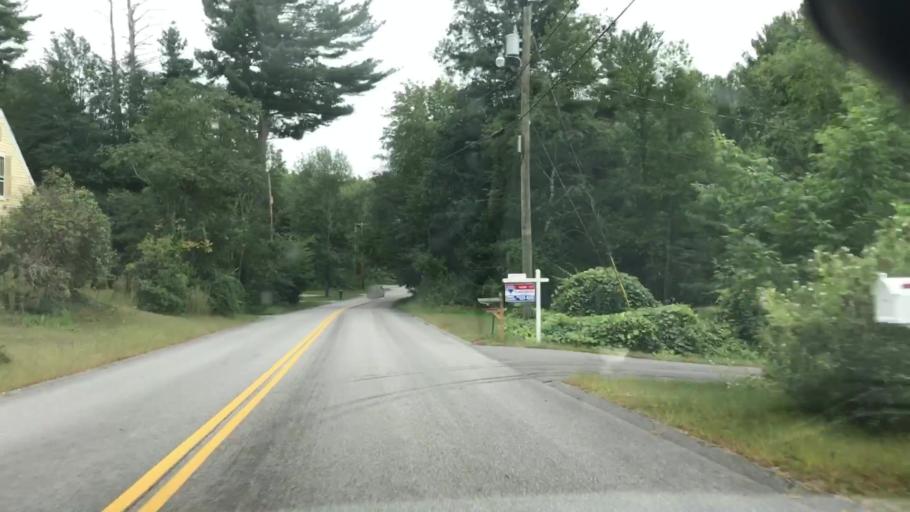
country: US
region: New Hampshire
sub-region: Hillsborough County
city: Hollis
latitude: 42.8088
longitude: -71.5569
